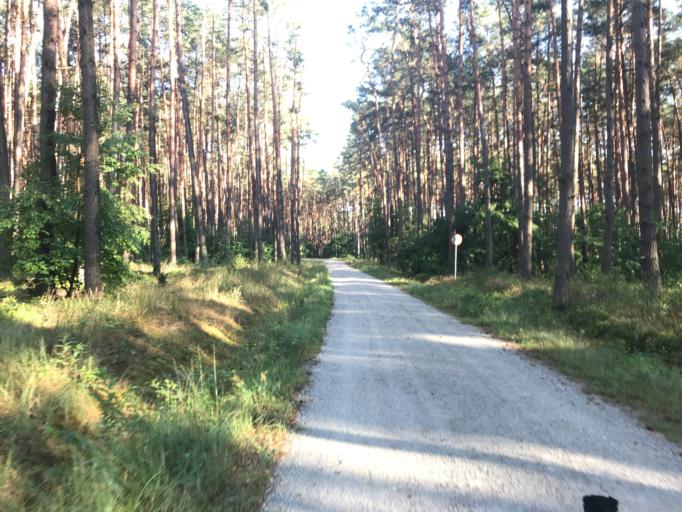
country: PL
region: Greater Poland Voivodeship
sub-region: Powiat szamotulski
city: Obrzycko
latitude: 52.7331
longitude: 16.5896
